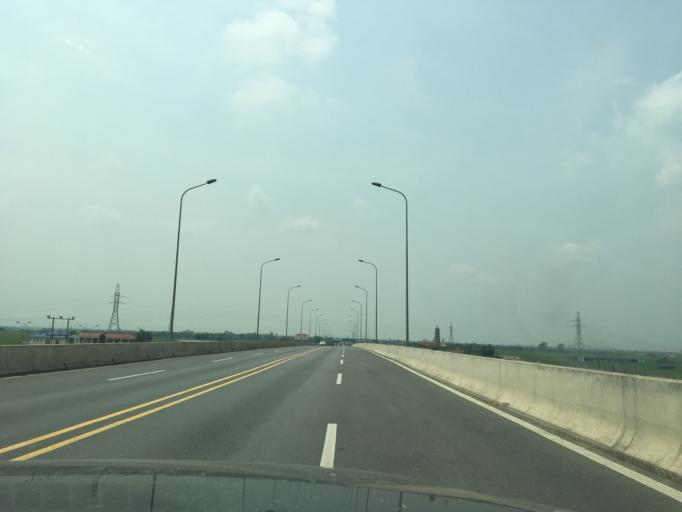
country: VN
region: Nam Dinh
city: Thi Tran Lam
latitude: 20.2860
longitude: 106.0143
